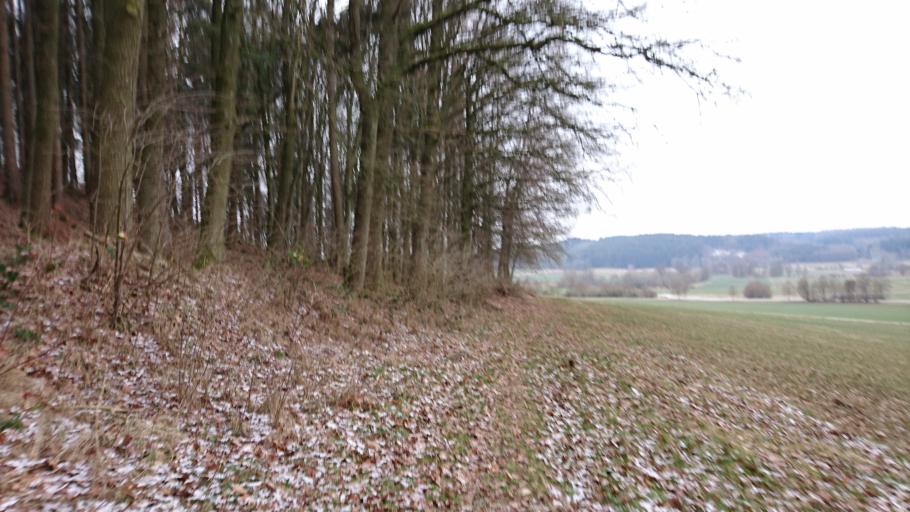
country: DE
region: Bavaria
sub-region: Swabia
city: Zusmarshausen
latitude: 48.4318
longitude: 10.6028
